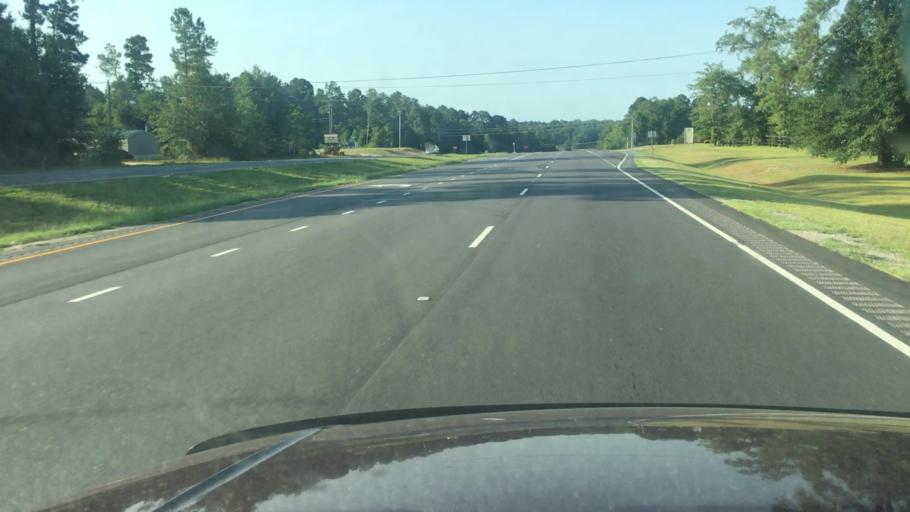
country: US
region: North Carolina
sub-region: Robeson County
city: Saint Pauls
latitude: 34.8654
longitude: -78.8502
